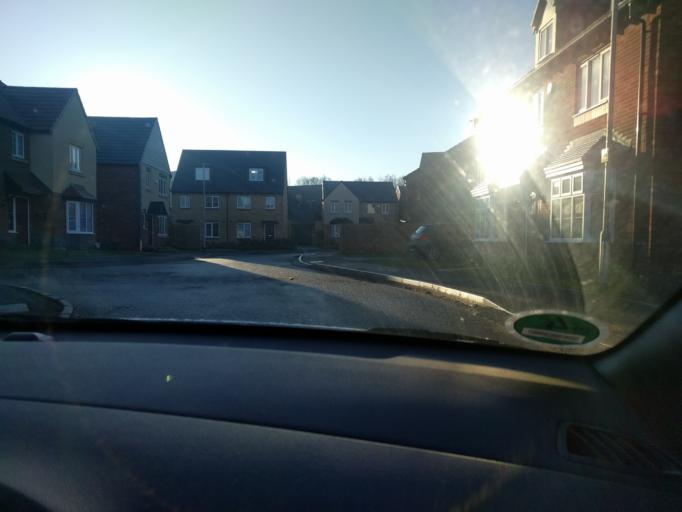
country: GB
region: England
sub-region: Telford and Wrekin
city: Wellington
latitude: 52.6937
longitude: -2.5156
